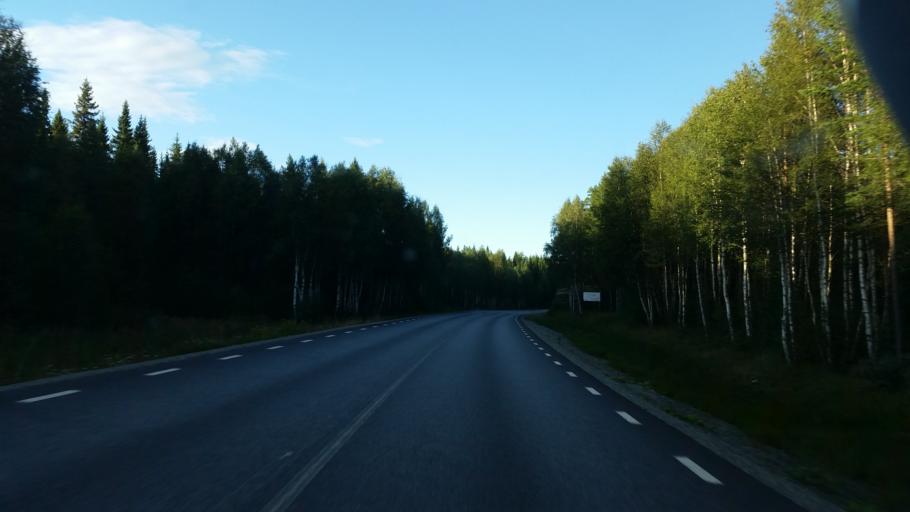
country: SE
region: Vaesterbotten
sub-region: Dorotea Kommun
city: Dorotea
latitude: 64.2375
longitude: 16.3107
